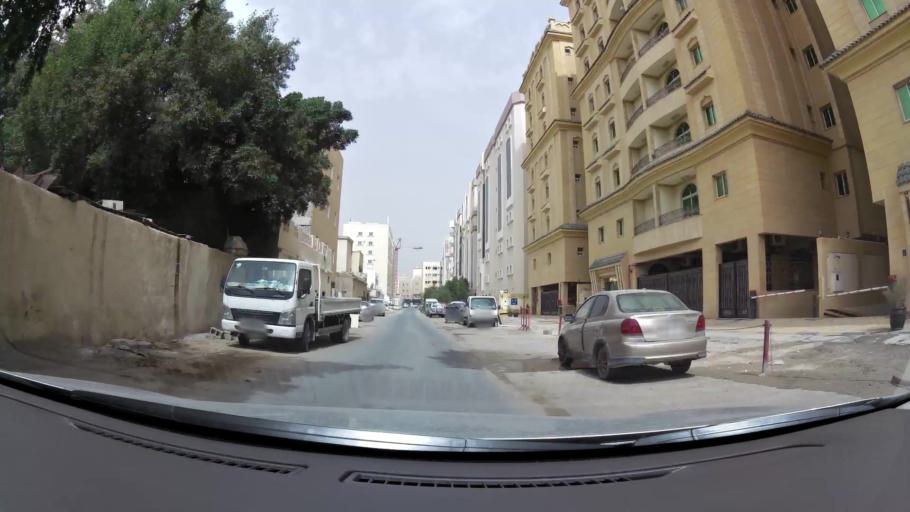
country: QA
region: Baladiyat ad Dawhah
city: Doha
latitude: 25.2693
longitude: 51.5452
